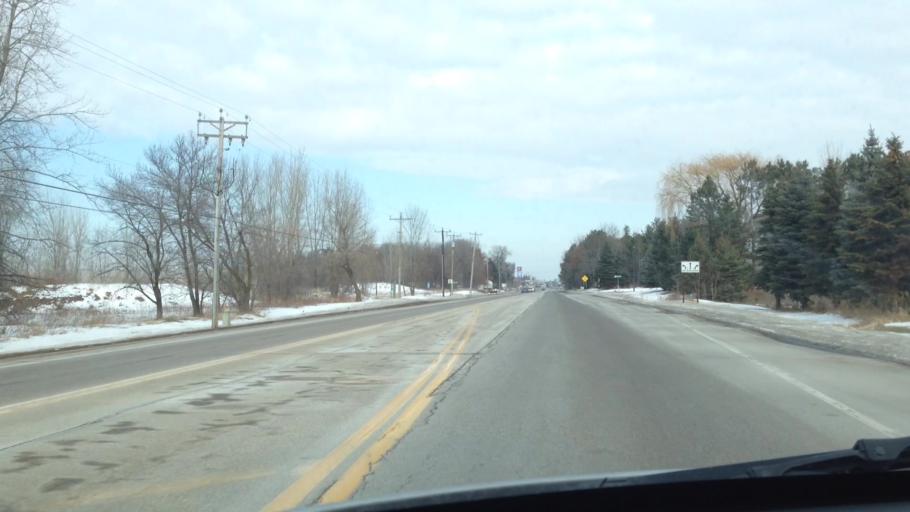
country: US
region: Minnesota
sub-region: Anoka County
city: Lino Lakes
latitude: 45.1717
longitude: -93.1186
